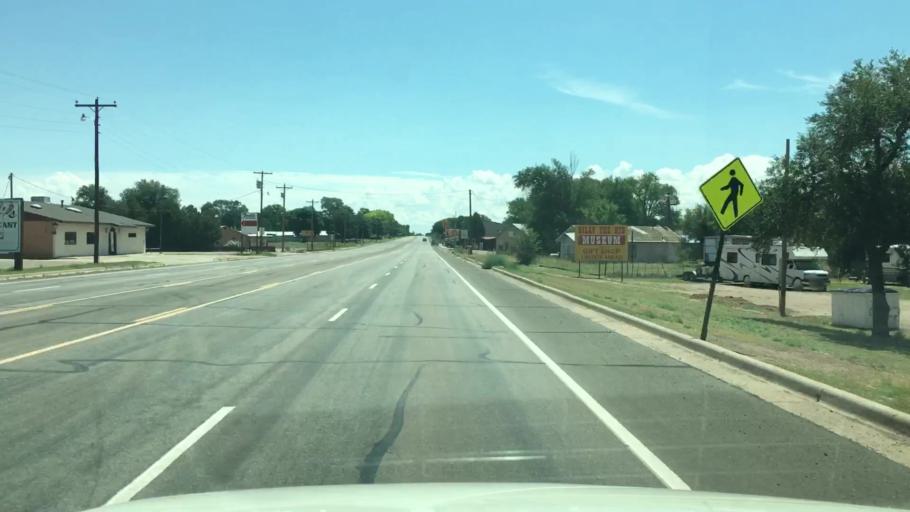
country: US
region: New Mexico
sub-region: De Baca County
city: Fort Sumner
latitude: 34.4673
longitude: -104.2317
